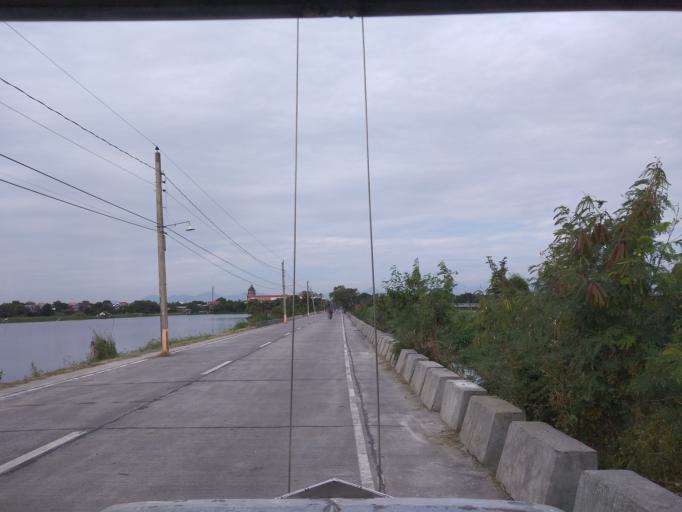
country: PH
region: Central Luzon
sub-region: Province of Pampanga
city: Lubao
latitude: 14.9385
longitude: 120.6074
